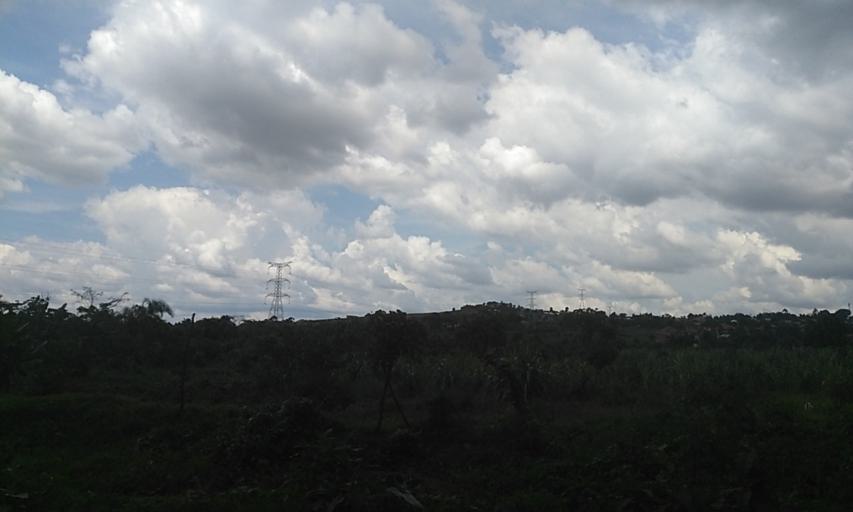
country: UG
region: Central Region
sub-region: Wakiso District
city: Wakiso
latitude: 0.3501
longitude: 32.4781
